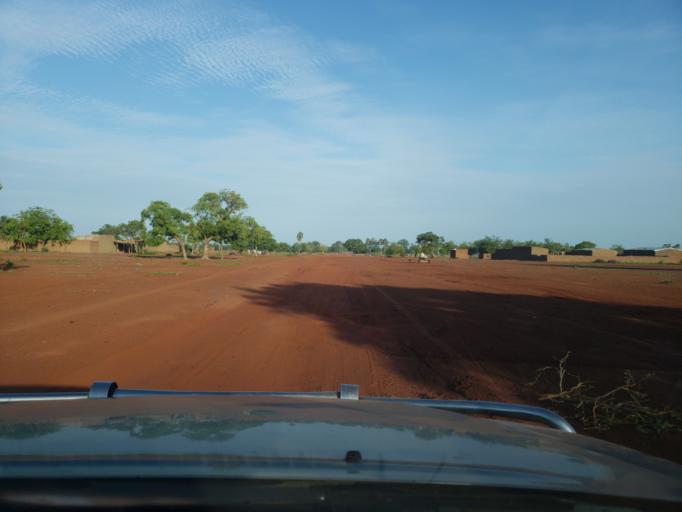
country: ML
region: Sikasso
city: Koutiala
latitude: 12.4047
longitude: -5.5342
